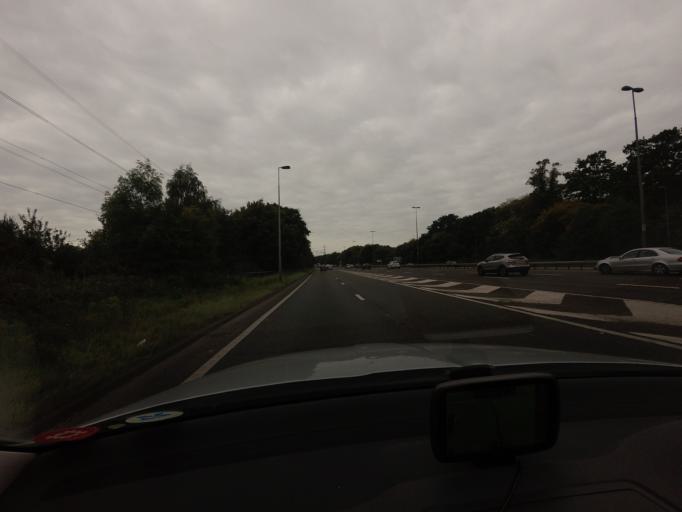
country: GB
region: England
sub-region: Surrey
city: Cobham
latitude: 51.3328
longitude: -0.4324
